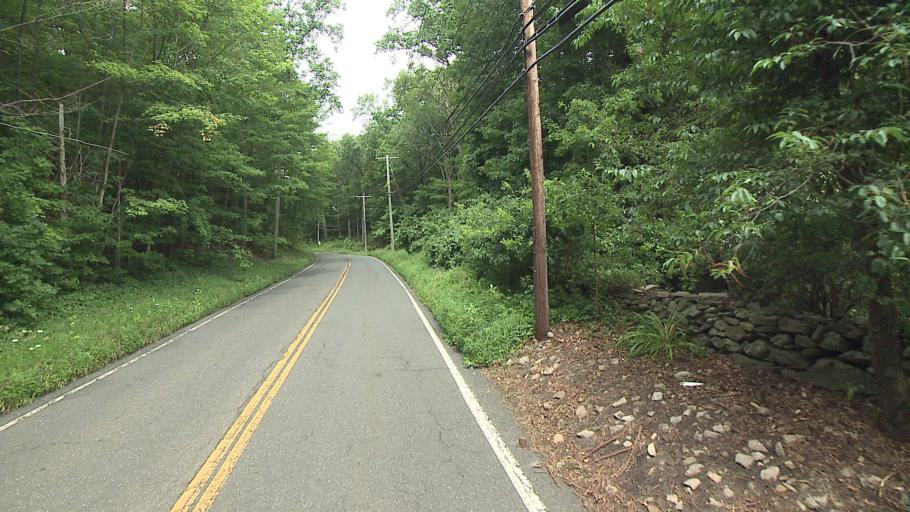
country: US
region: Connecticut
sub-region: Litchfield County
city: New Milford
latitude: 41.5413
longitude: -73.3674
